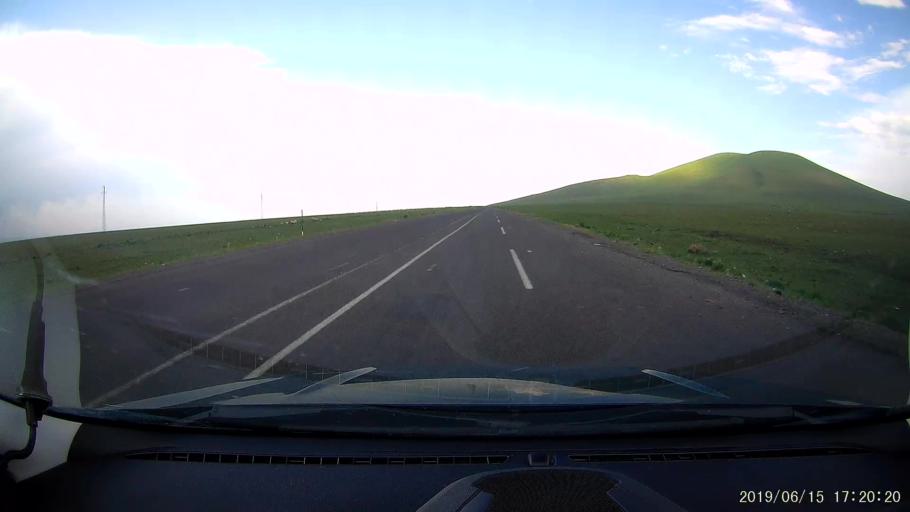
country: TR
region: Kars
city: Kars
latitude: 40.6161
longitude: 43.2989
